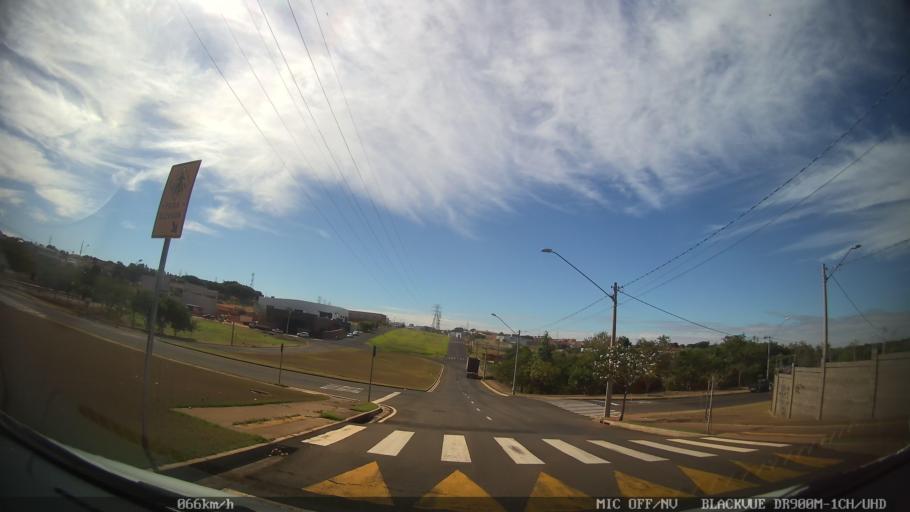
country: BR
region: Sao Paulo
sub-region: Sao Jose Do Rio Preto
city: Sao Jose do Rio Preto
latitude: -20.8486
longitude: -49.3734
